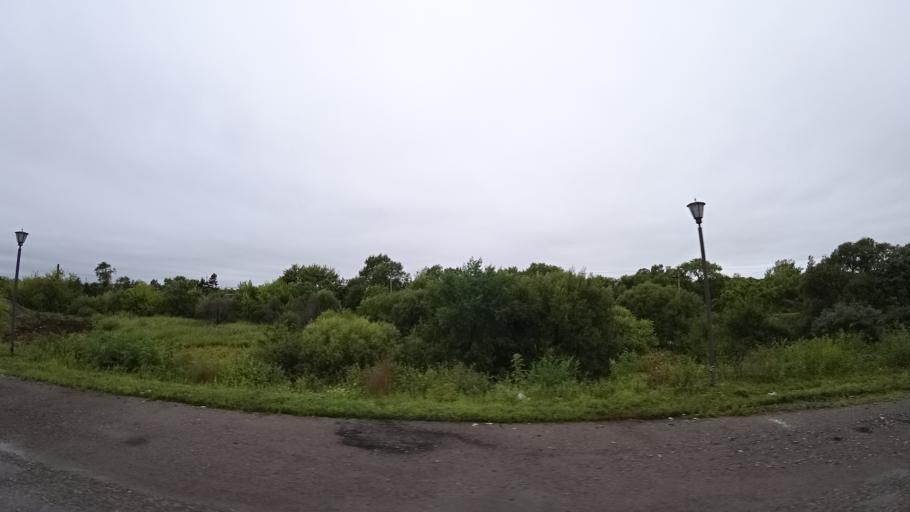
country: RU
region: Primorskiy
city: Monastyrishche
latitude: 44.2160
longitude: 132.4504
